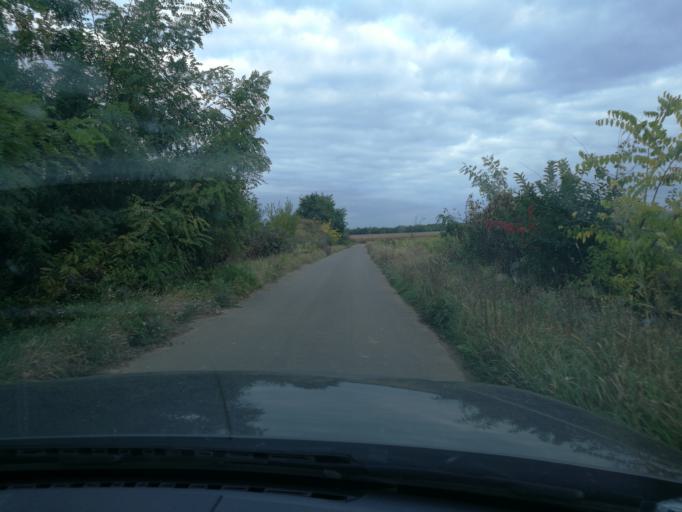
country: HU
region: Szabolcs-Szatmar-Bereg
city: Apagy
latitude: 47.9965
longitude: 21.9023
